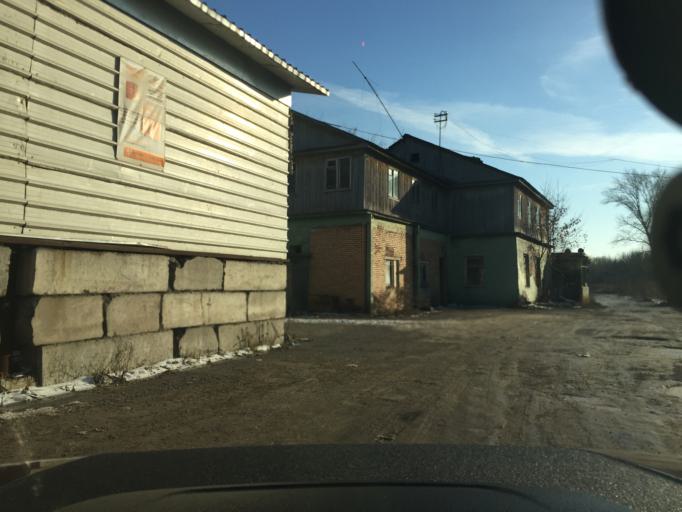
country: RU
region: Tula
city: Tula
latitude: 54.1767
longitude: 37.7011
